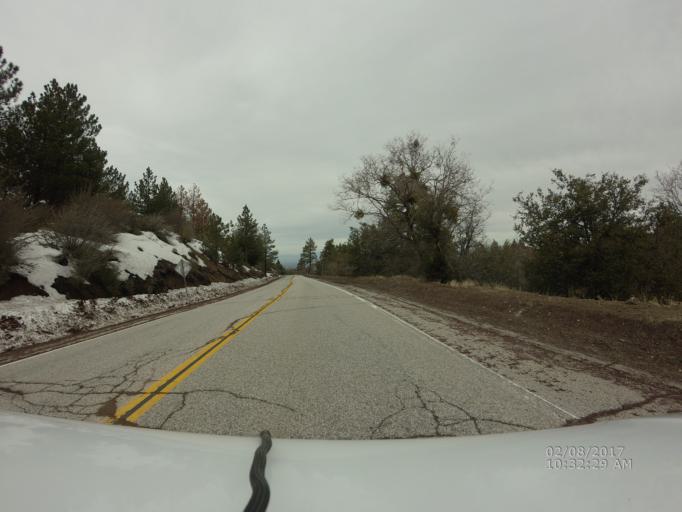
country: US
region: California
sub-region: San Bernardino County
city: Pinon Hills
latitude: 34.3987
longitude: -117.7326
